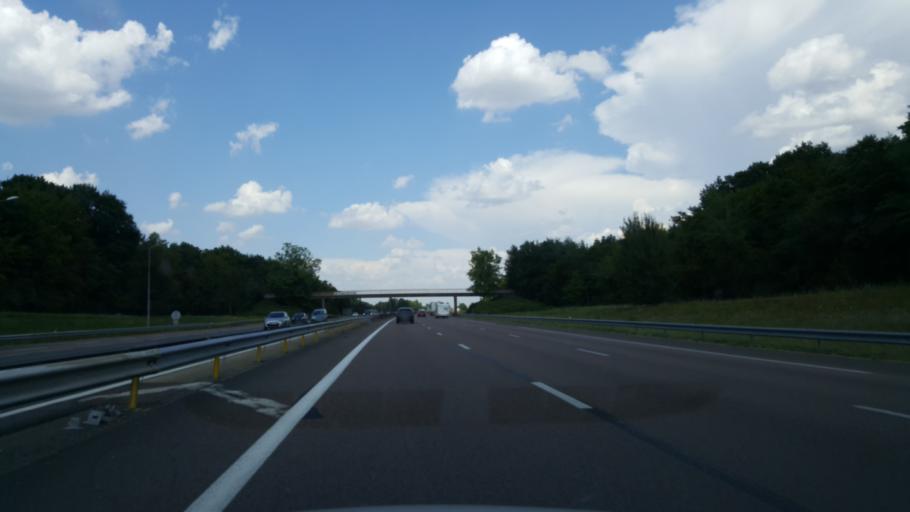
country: FR
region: Bourgogne
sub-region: Departement de la Cote-d'Or
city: Bligny-les-Beaune
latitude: 46.9700
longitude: 4.8398
